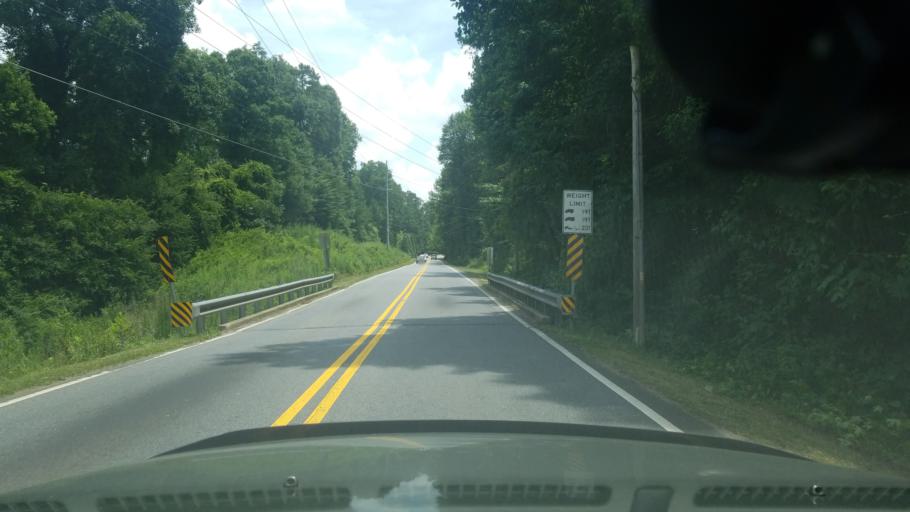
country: US
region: Georgia
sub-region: Fulton County
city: Milton
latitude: 34.1649
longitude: -84.2729
